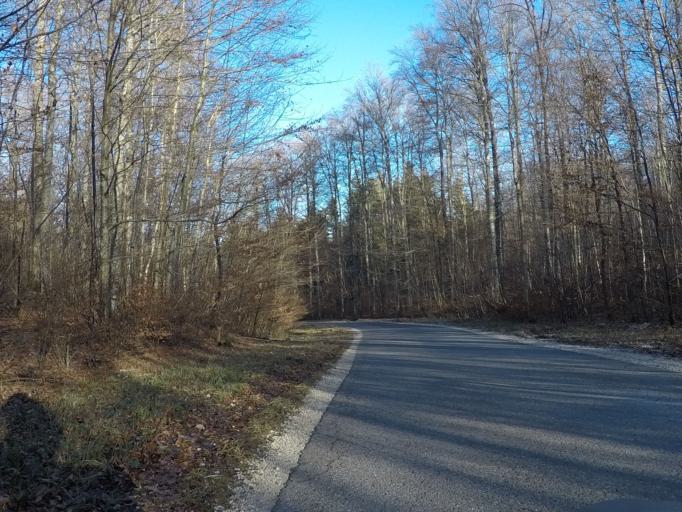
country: DE
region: Baden-Wuerttemberg
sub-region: Tuebingen Region
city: Sankt Johann
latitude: 48.4368
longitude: 9.2956
